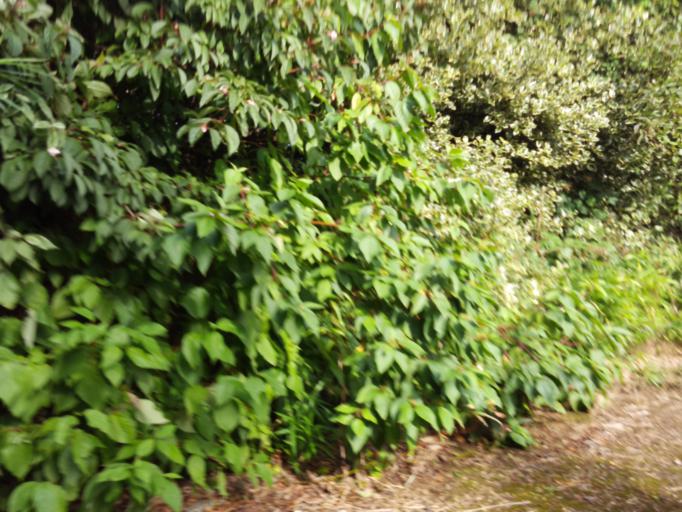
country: GB
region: Scotland
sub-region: West Lothian
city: Livingston
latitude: 55.8914
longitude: -3.5359
